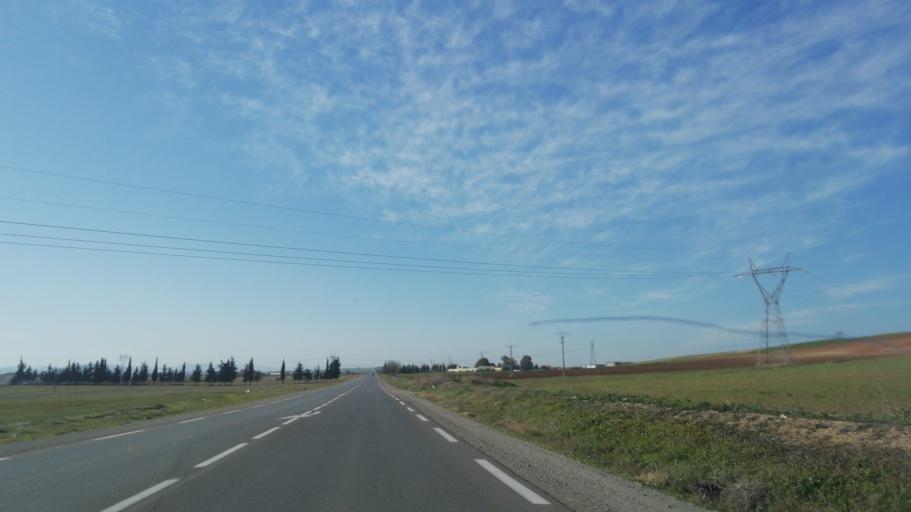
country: DZ
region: Tlemcen
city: Ouled Mimoun
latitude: 35.0458
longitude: -0.8385
